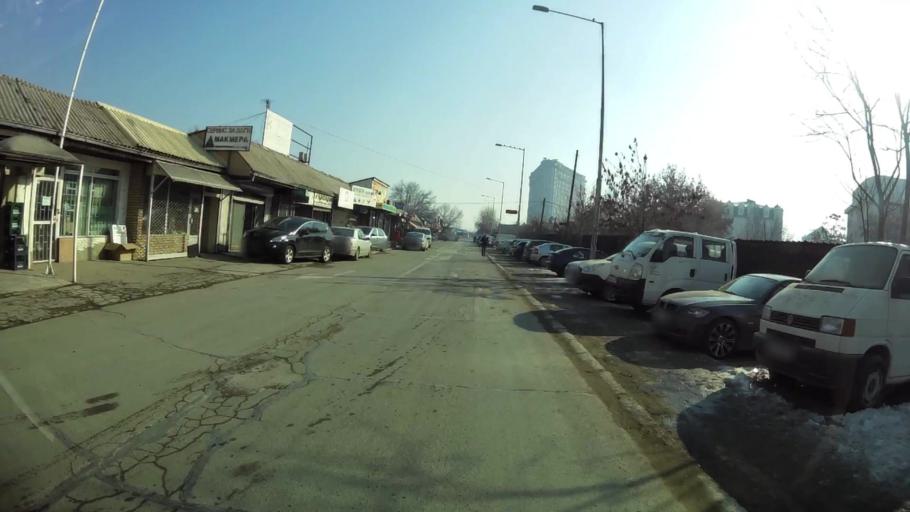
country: MK
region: Karpos
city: Skopje
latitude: 41.9875
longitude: 21.4353
